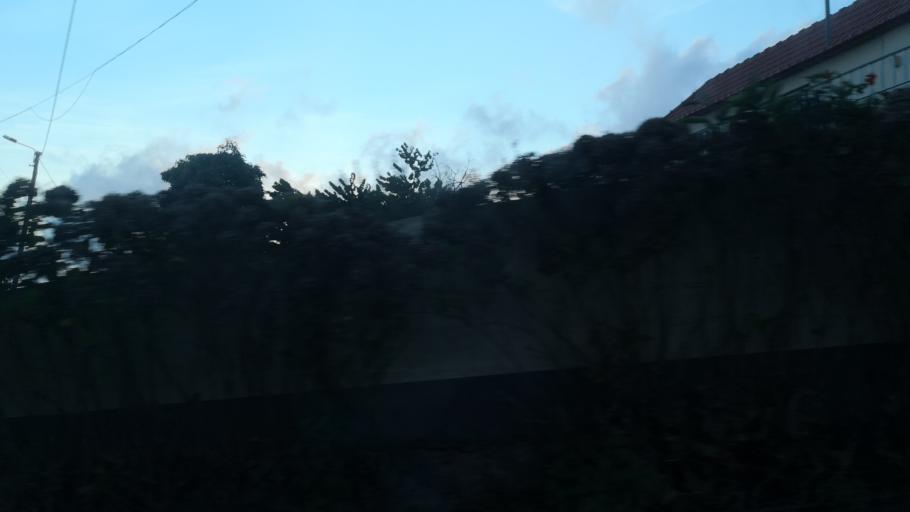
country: PT
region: Madeira
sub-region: Santa Cruz
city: Camacha
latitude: 32.6796
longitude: -16.8264
